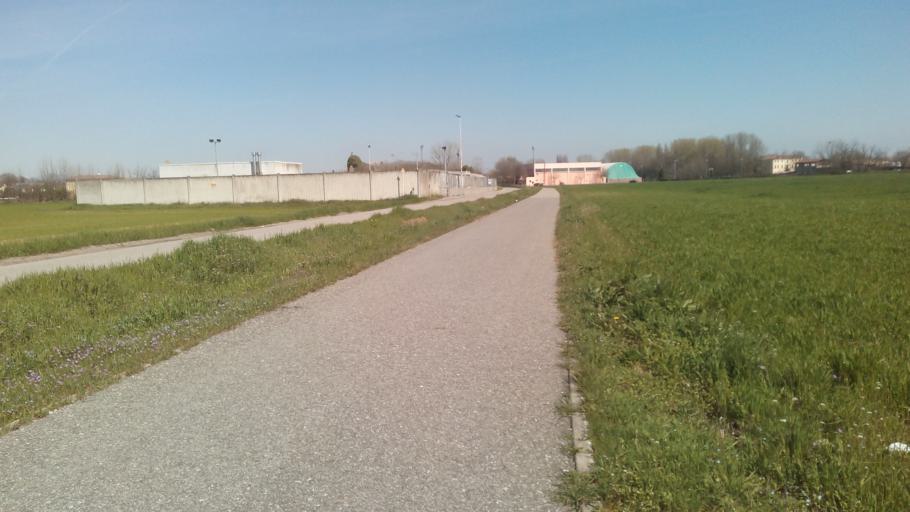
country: IT
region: Lombardy
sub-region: Provincia di Mantova
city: Goito
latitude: 45.2443
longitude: 10.6690
